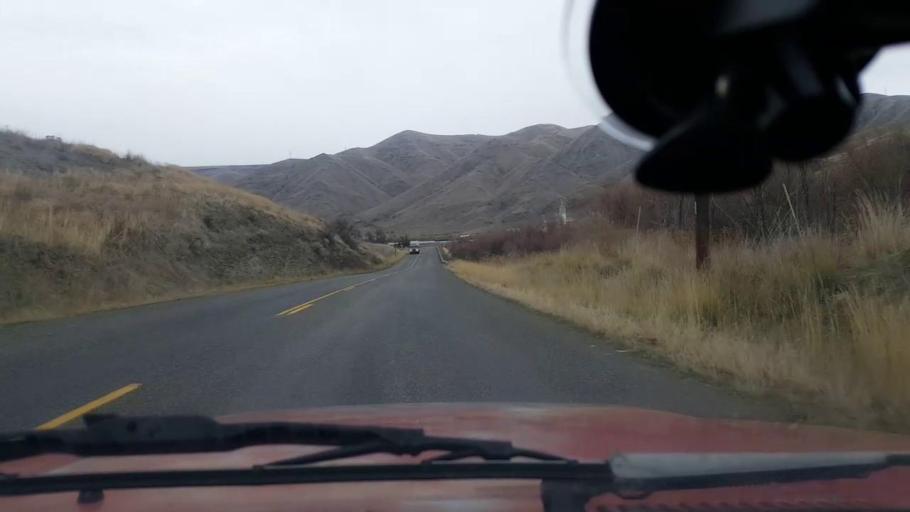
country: US
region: Washington
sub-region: Asotin County
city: Clarkston Heights-Vineland
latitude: 46.4162
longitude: -117.1139
